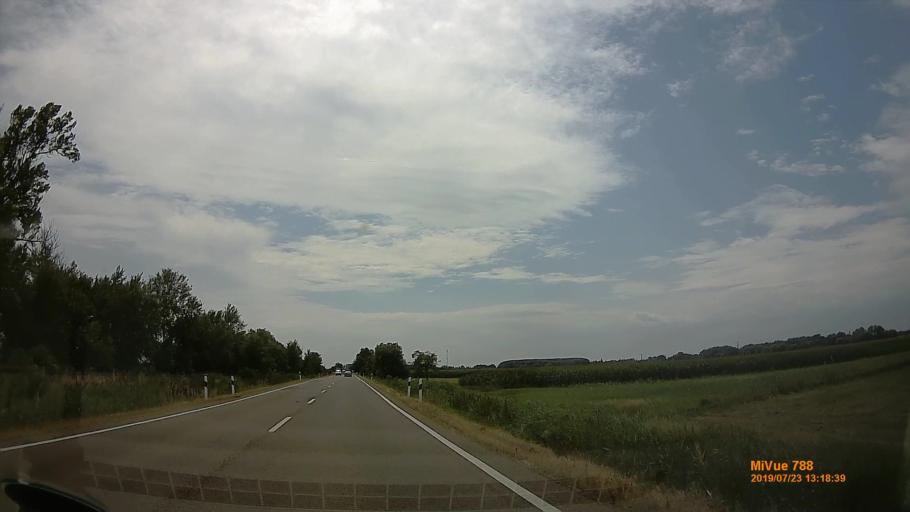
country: HU
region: Hajdu-Bihar
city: Polgar
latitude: 47.8827
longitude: 21.1476
